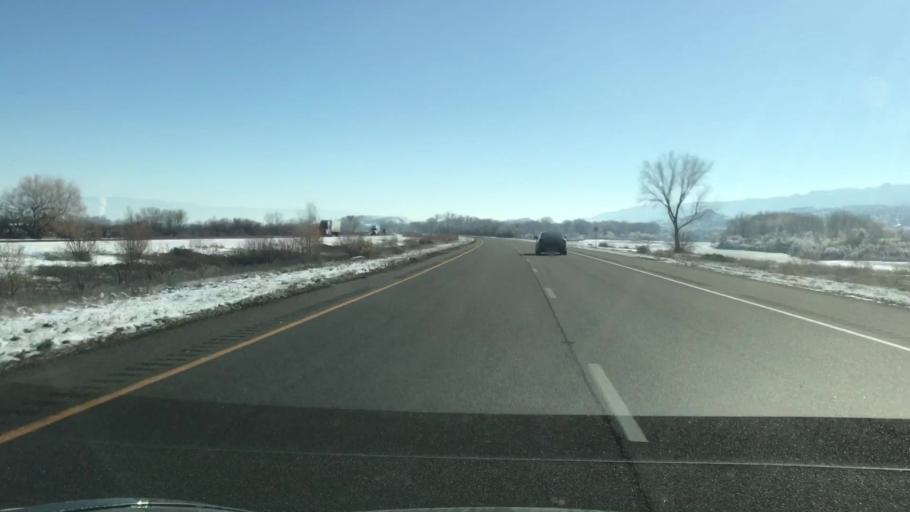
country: US
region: Colorado
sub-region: Mesa County
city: Loma
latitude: 39.1697
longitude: -108.7932
